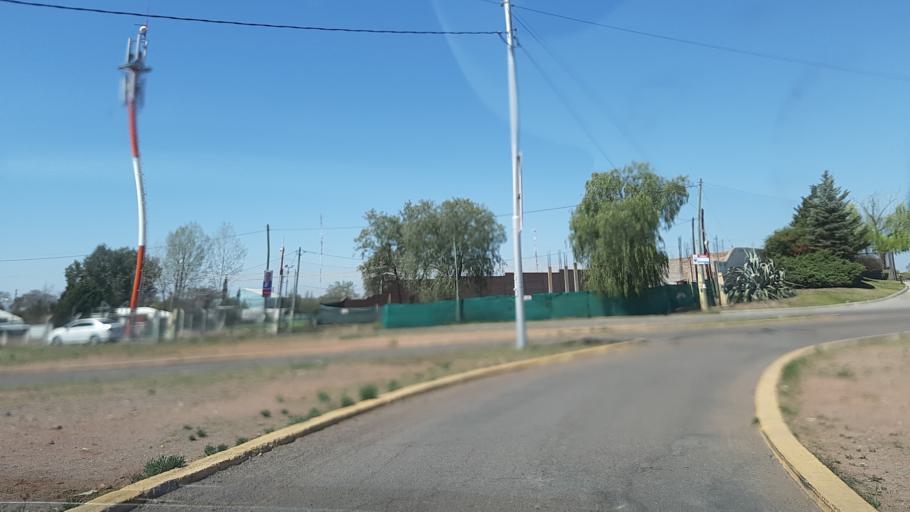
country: AR
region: Mendoza
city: Lujan de Cuyo
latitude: -33.0155
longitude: -68.9312
